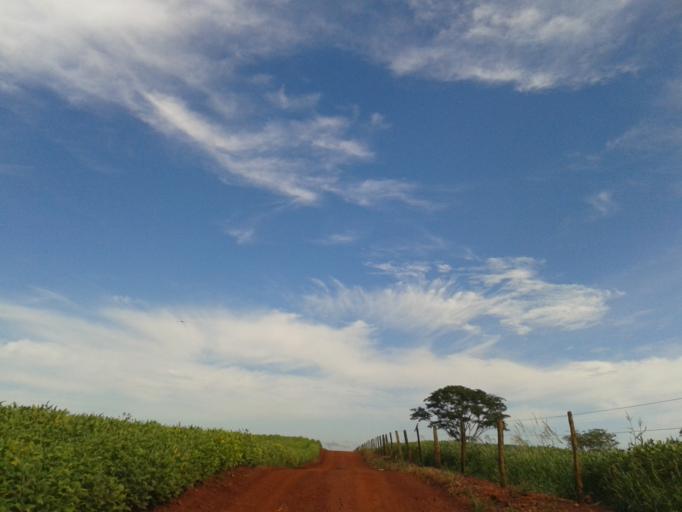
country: BR
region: Minas Gerais
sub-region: Capinopolis
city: Capinopolis
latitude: -18.6418
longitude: -49.7163
